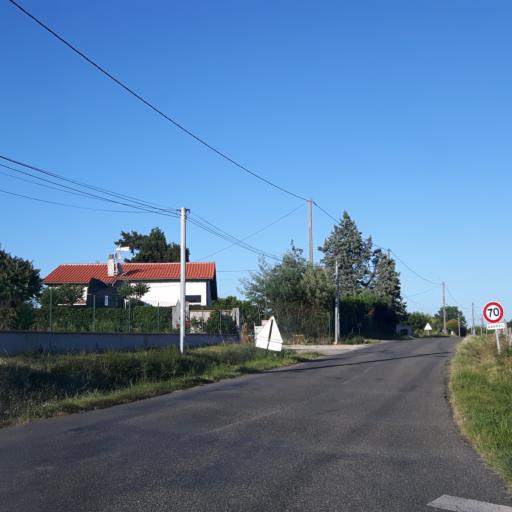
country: FR
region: Midi-Pyrenees
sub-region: Departement de la Haute-Garonne
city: Fronton
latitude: 43.8158
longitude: 1.3866
